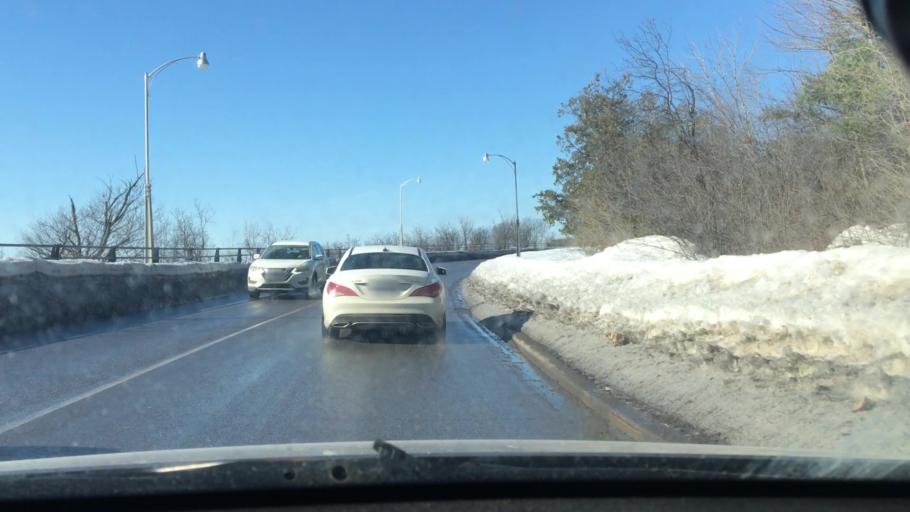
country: CA
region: Quebec
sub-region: Outaouais
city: Gatineau
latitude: 45.4527
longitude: -75.6881
